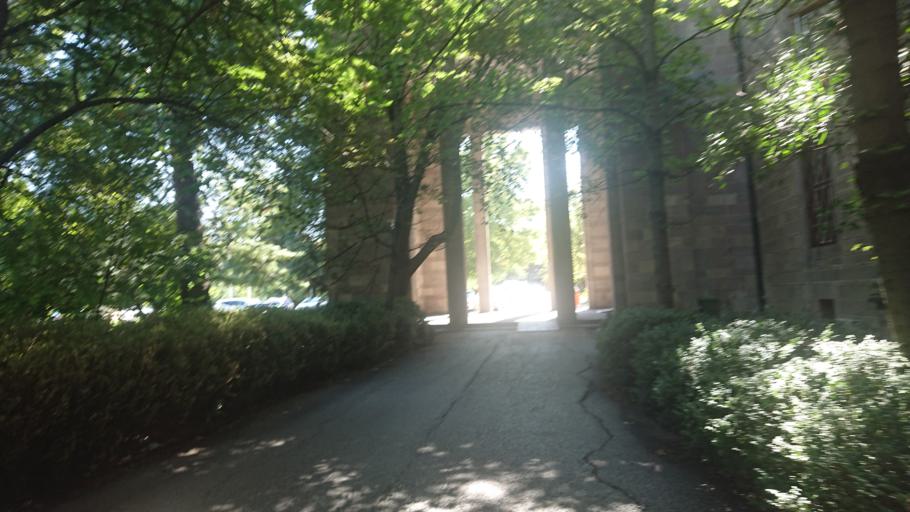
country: TR
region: Ankara
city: Ankara
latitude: 39.9347
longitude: 32.8316
